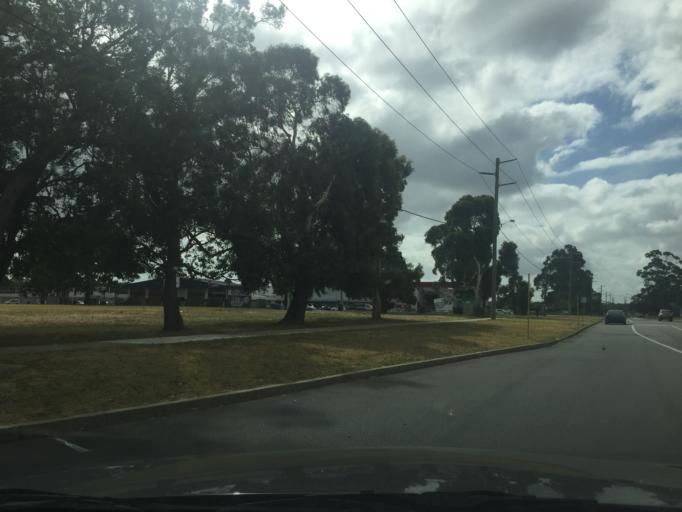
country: AU
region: Western Australia
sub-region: Gosnells
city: Maddington
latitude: -32.0535
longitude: 115.9818
